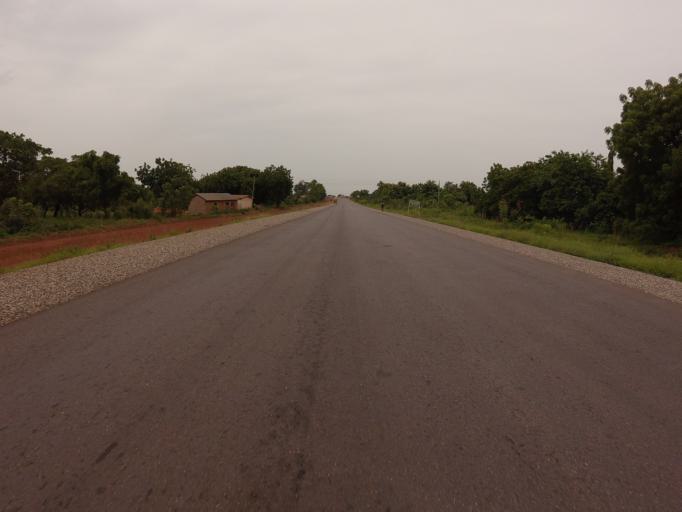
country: GH
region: Northern
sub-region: Yendi
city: Yendi
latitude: 9.3075
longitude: 0.0169
